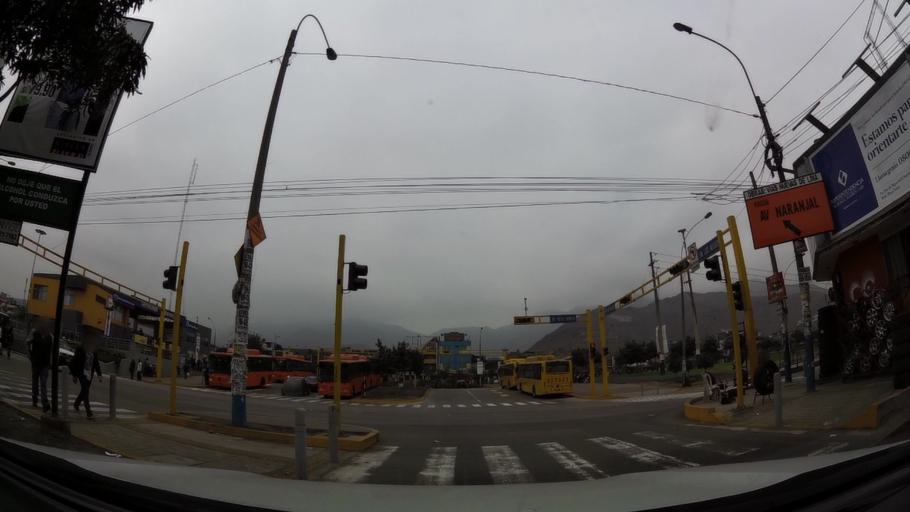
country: PE
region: Lima
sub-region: Lima
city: Independencia
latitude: -11.9832
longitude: -77.0590
